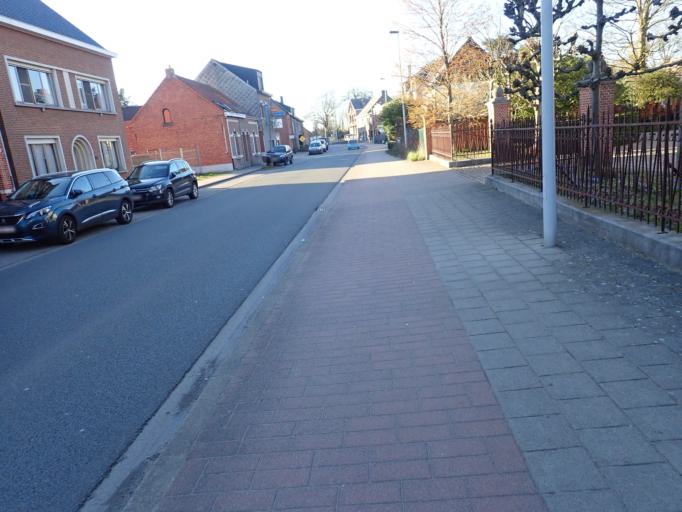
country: BE
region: Flanders
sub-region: Provincie Antwerpen
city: Nijlen
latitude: 51.1357
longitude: 4.6847
